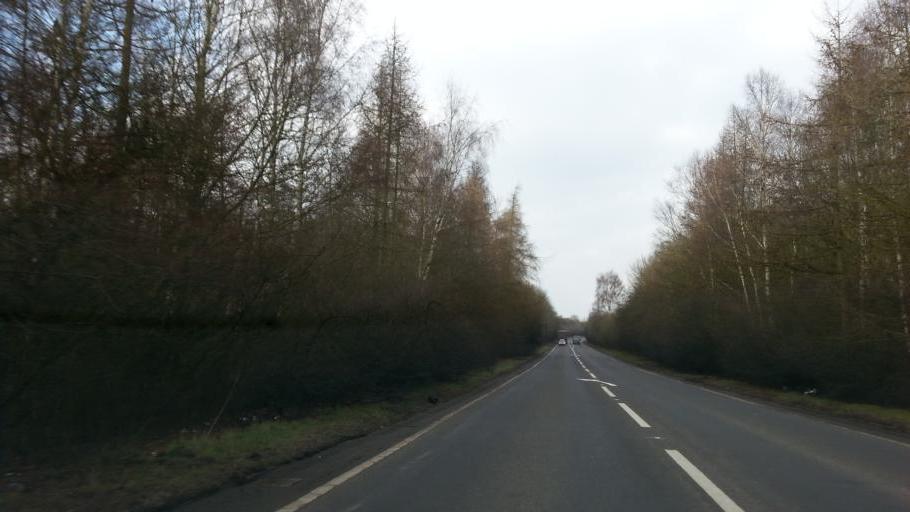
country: GB
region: England
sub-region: District of Rutland
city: South Luffenham
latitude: 52.5323
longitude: -0.5907
